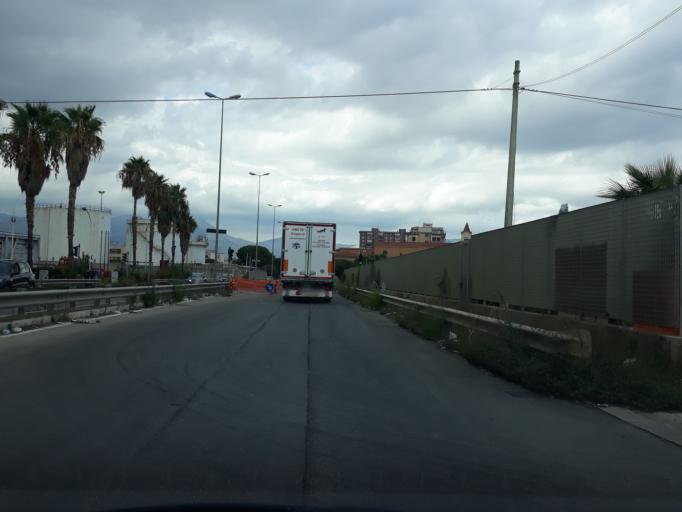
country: IT
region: Sicily
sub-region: Palermo
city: Ciaculli
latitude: 38.0926
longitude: 13.4073
